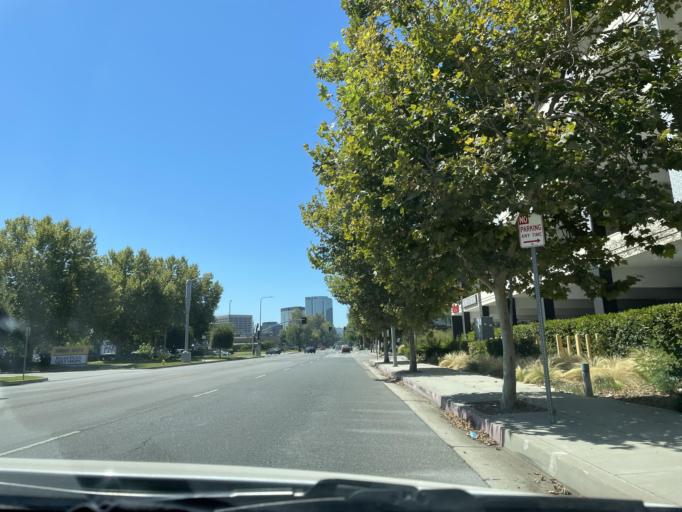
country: US
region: California
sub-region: Los Angeles County
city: Canoga Park
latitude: 34.1890
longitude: -118.6016
